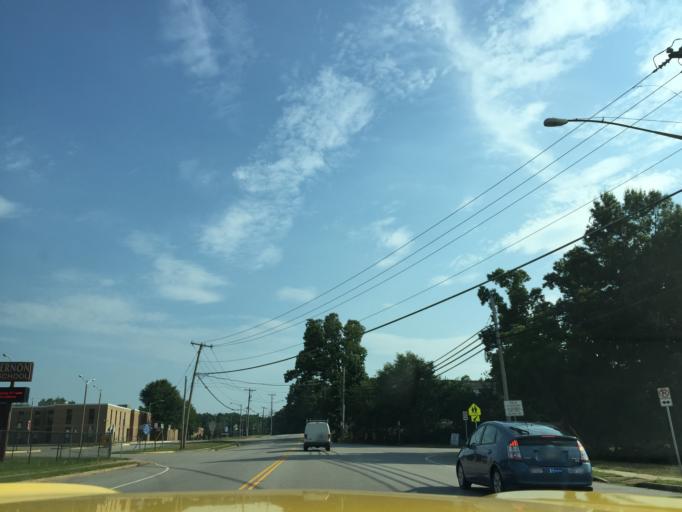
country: US
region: Virginia
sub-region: Fairfax County
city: Mount Vernon
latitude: 38.7292
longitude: -77.0937
